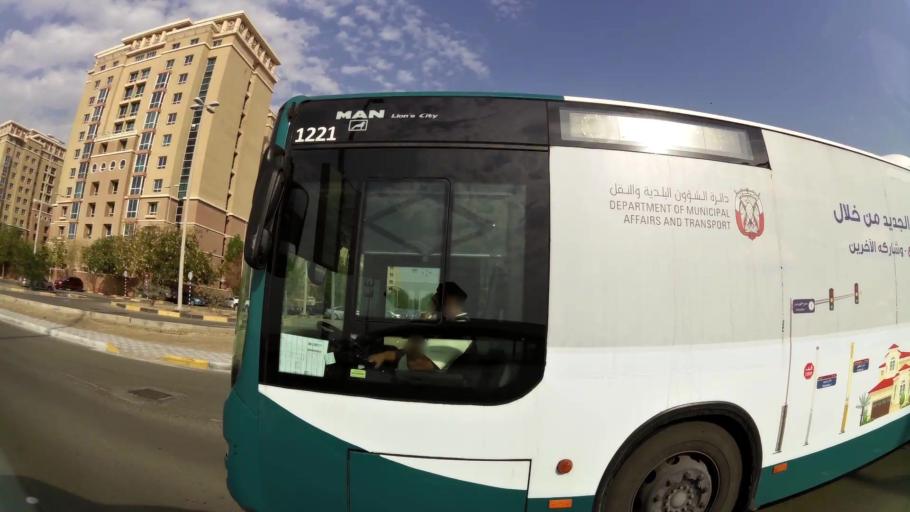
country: AE
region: Abu Dhabi
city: Abu Dhabi
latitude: 24.3703
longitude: 54.5359
